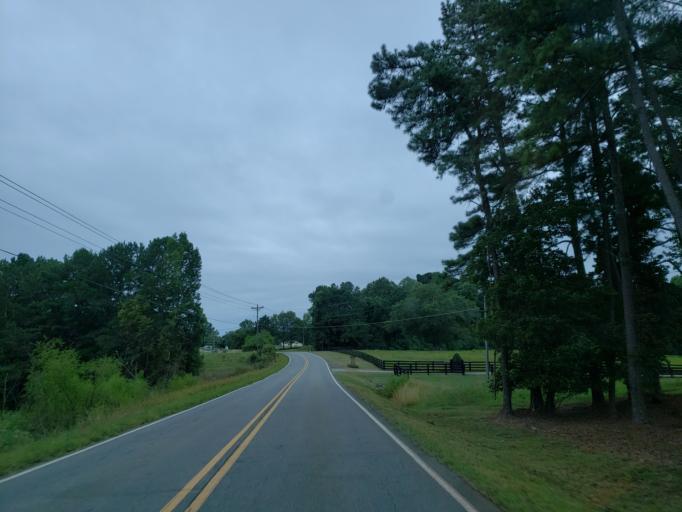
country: US
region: Georgia
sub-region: Cherokee County
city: Canton
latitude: 34.3497
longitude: -84.4899
